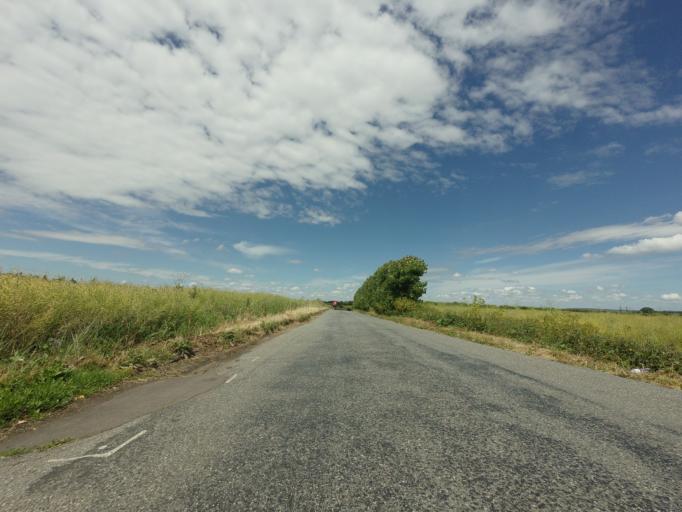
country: GB
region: England
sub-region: Kent
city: Strood
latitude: 51.4252
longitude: 0.4773
